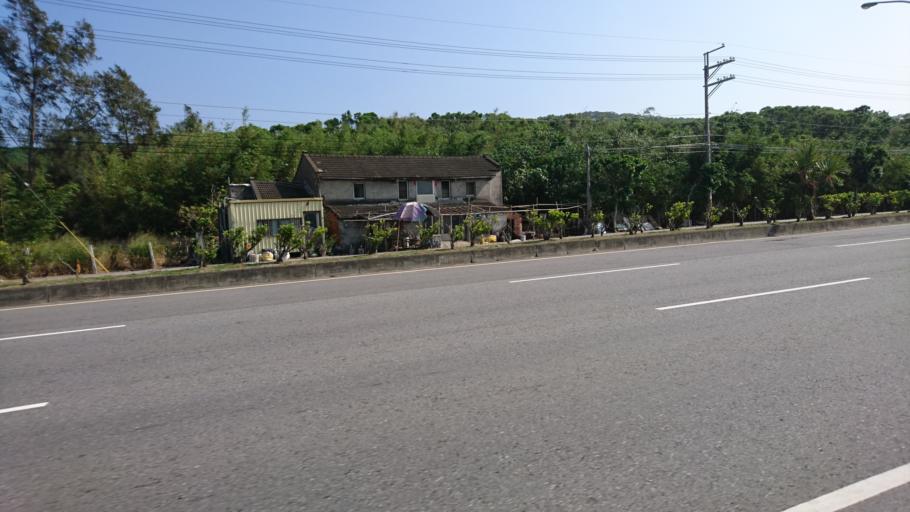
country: TW
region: Taiwan
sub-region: Miaoli
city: Miaoli
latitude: 24.5121
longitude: 120.6903
